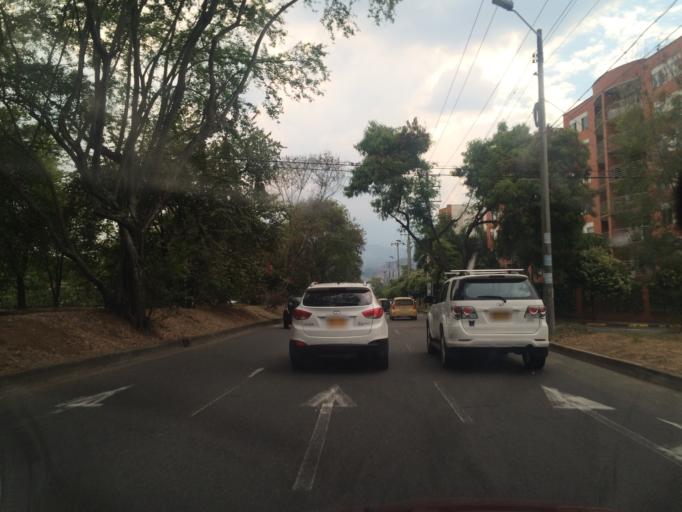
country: CO
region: Valle del Cauca
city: Cali
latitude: 3.3877
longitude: -76.5336
